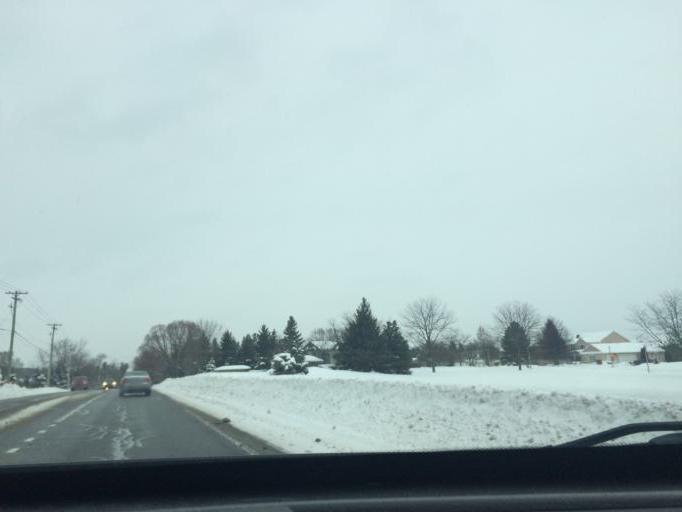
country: US
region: New York
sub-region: Monroe County
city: Fairport
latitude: 43.1196
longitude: -77.4415
